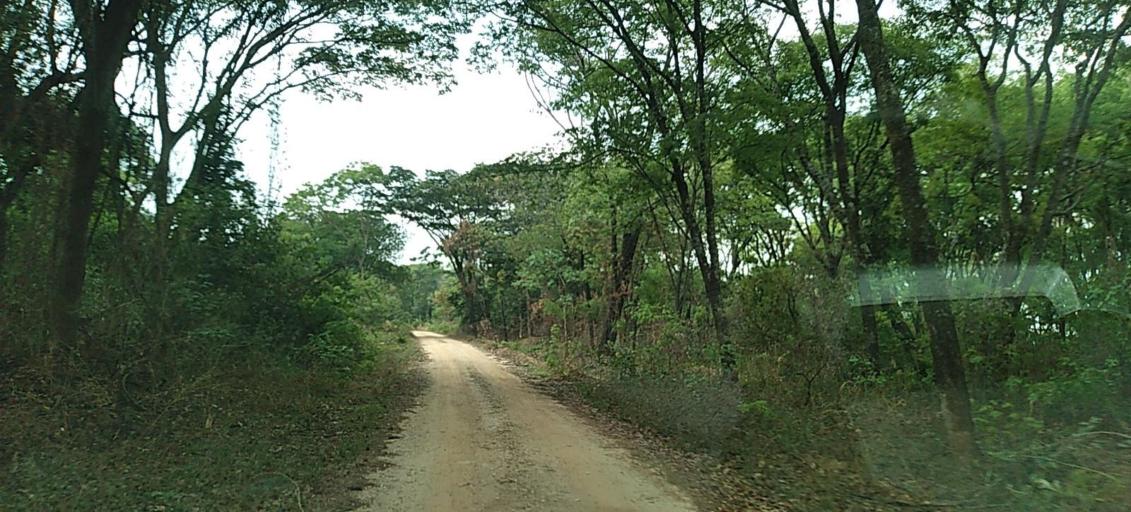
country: ZM
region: Copperbelt
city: Chingola
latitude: -12.7500
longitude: 27.7251
